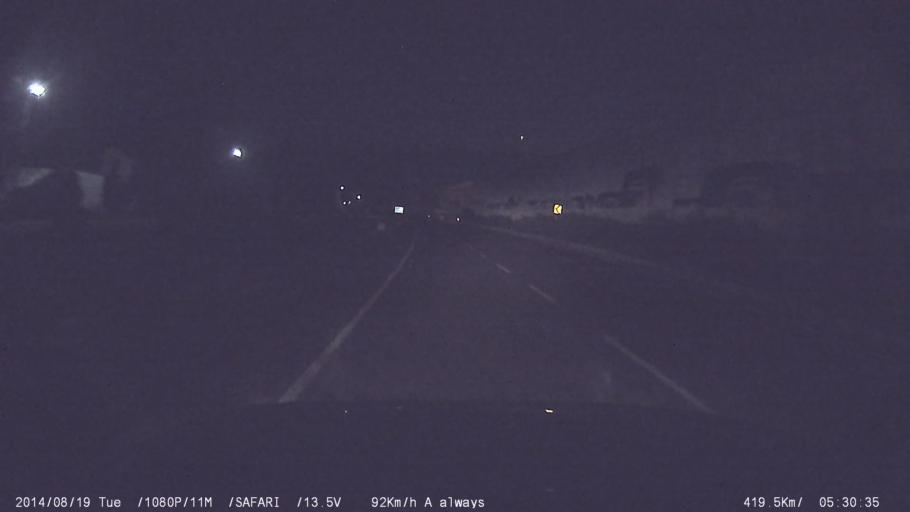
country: IN
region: Tamil Nadu
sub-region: Salem
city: Salem
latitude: 11.6120
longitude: 78.1037
